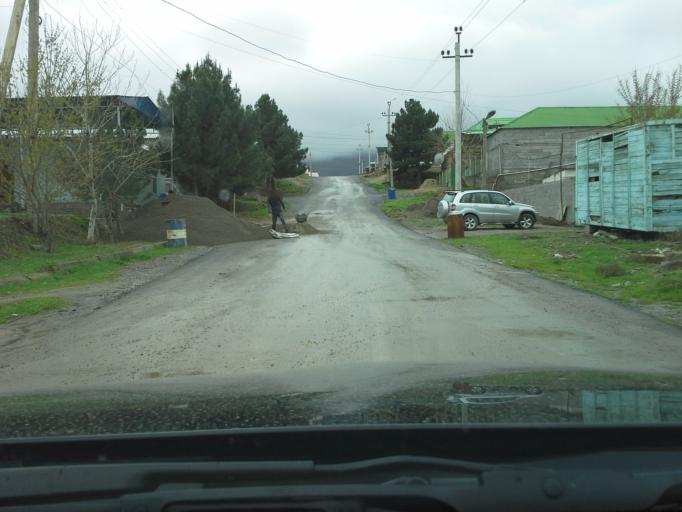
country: TM
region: Ahal
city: Abadan
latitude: 37.9625
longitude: 58.2040
